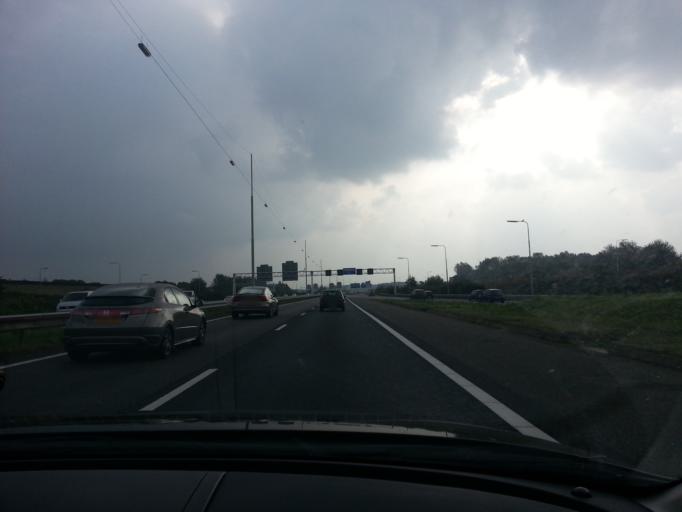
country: NL
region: South Holland
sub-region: Gemeente Den Haag
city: Ypenburg
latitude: 52.0530
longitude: 4.3647
